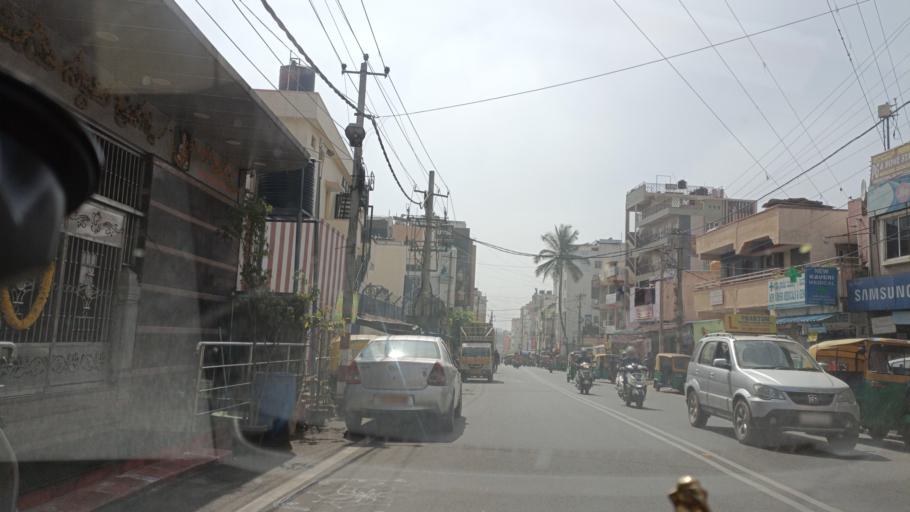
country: IN
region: Karnataka
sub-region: Bangalore Urban
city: Bangalore
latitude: 12.9296
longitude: 77.6095
